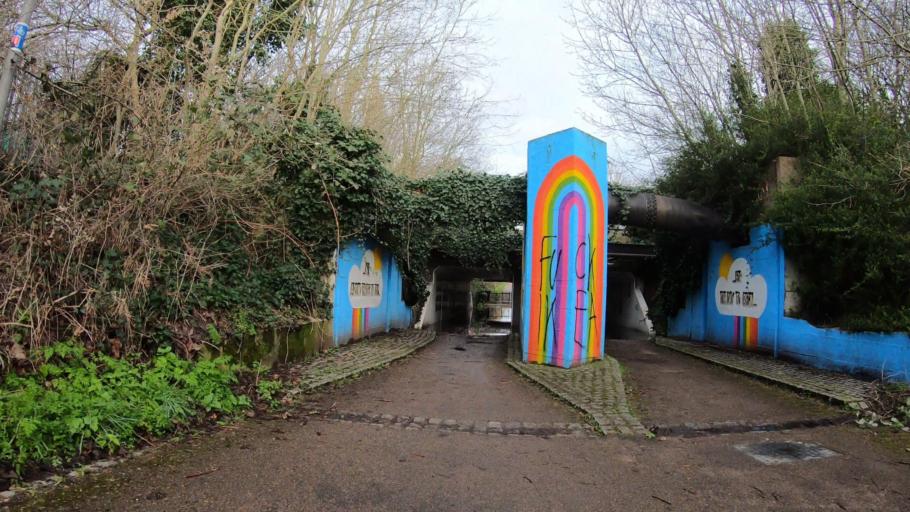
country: GB
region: England
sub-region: Greater London
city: Hackney
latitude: 51.5594
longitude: -0.0261
